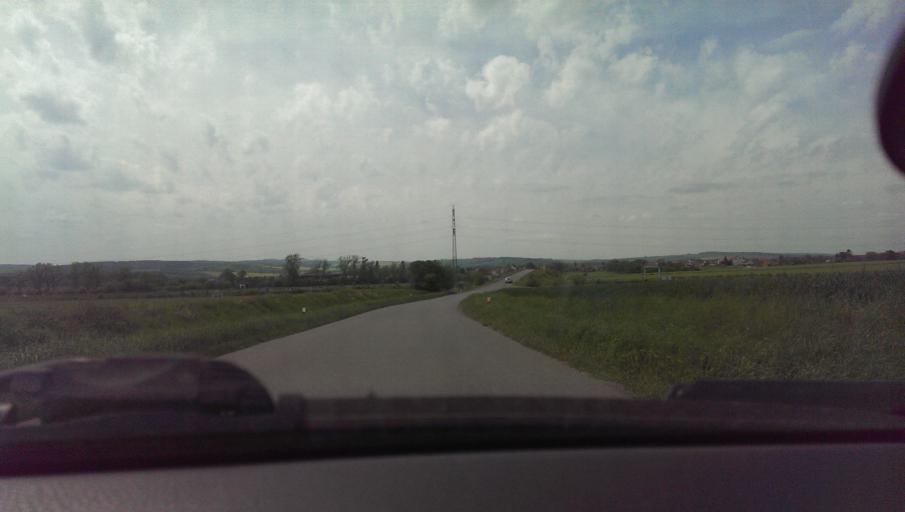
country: CZ
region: Zlin
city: Tlumacov
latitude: 49.2547
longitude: 17.5188
